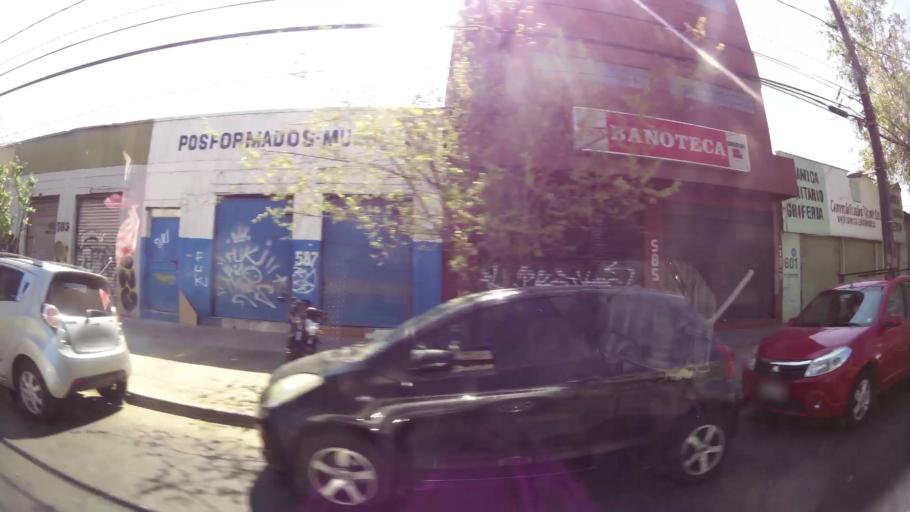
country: CL
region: Santiago Metropolitan
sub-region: Provincia de Santiago
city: Santiago
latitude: -33.4726
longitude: -70.6389
